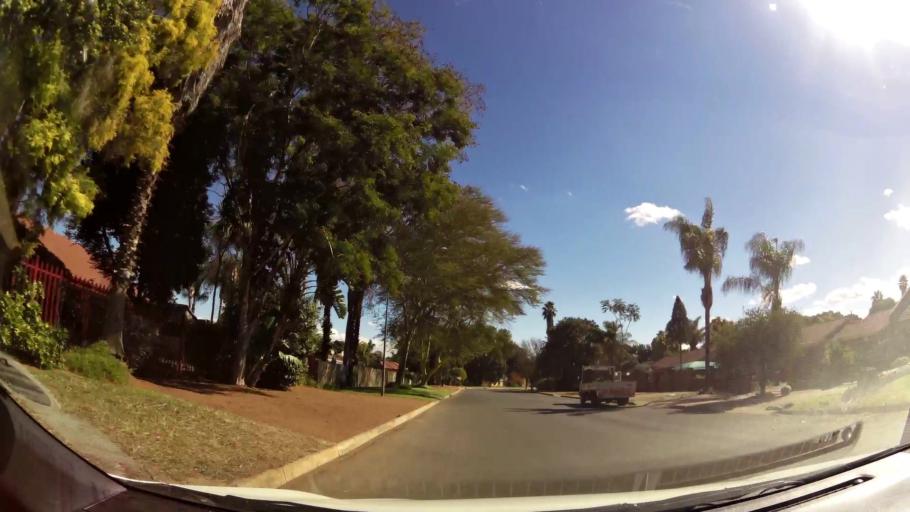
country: ZA
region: Limpopo
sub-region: Capricorn District Municipality
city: Polokwane
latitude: -23.9133
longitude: 29.4880
